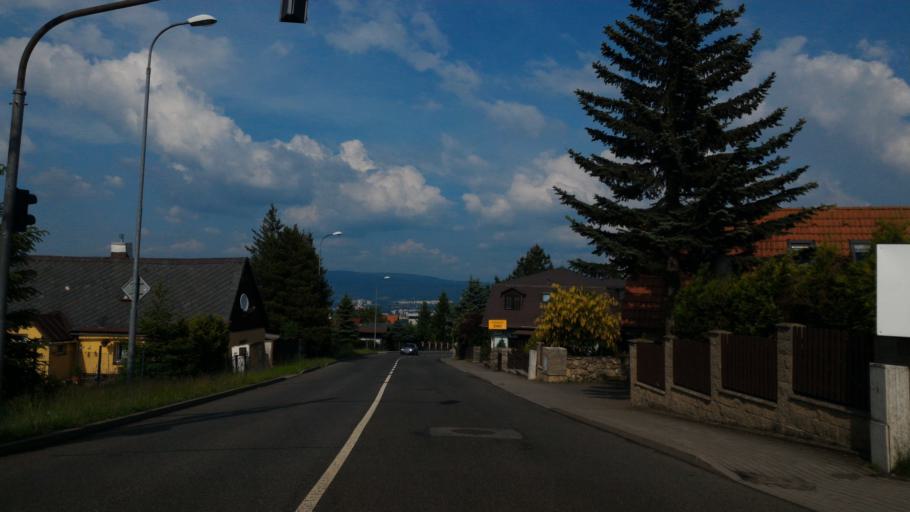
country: CZ
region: Liberecky
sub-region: Okres Liberec
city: Liberec
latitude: 50.7387
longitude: 15.0142
